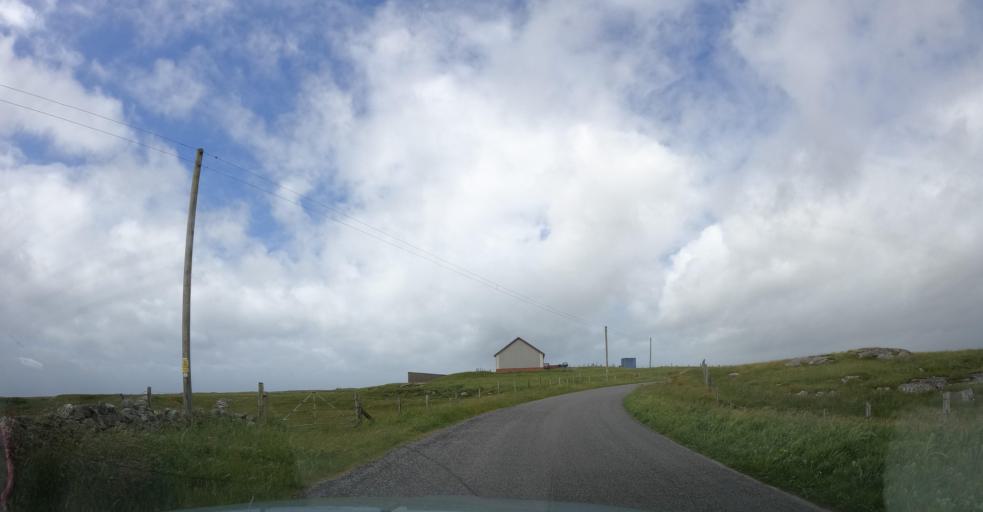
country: GB
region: Scotland
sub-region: Eilean Siar
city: Isle of South Uist
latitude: 57.2528
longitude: -7.4065
